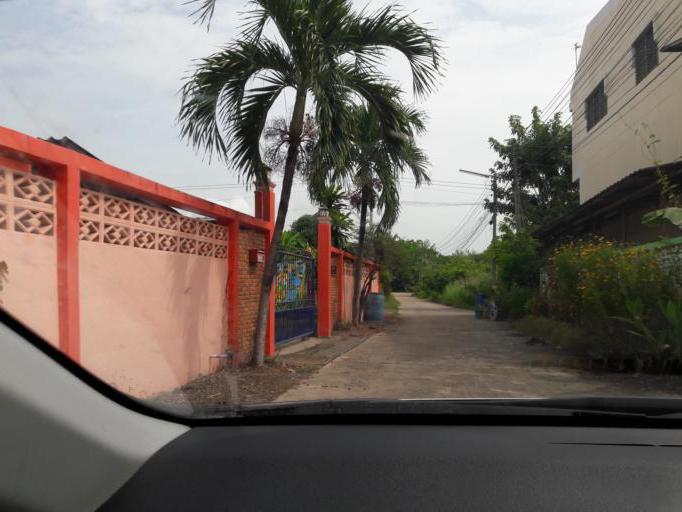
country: TH
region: Ratchaburi
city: Ratchaburi
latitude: 13.5200
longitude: 99.7957
